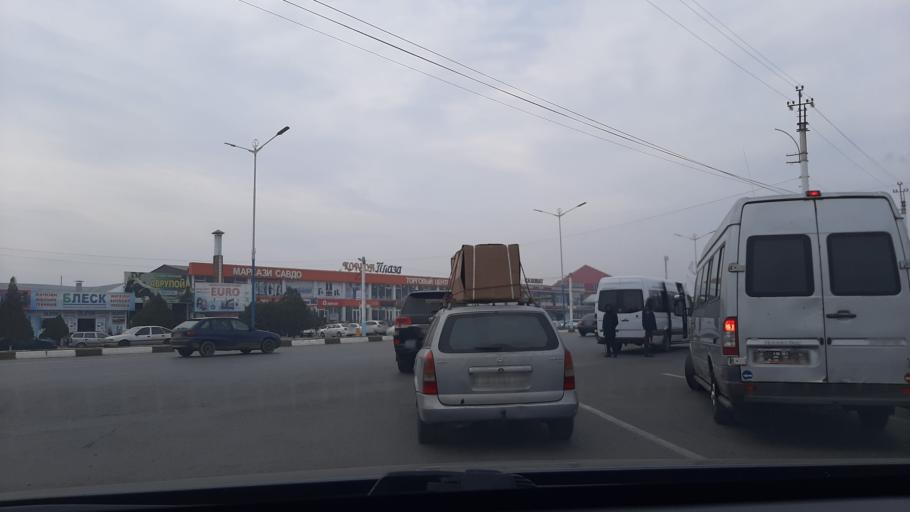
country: TJ
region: Viloyati Sughd
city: Chkalov
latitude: 40.2451
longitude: 69.6996
